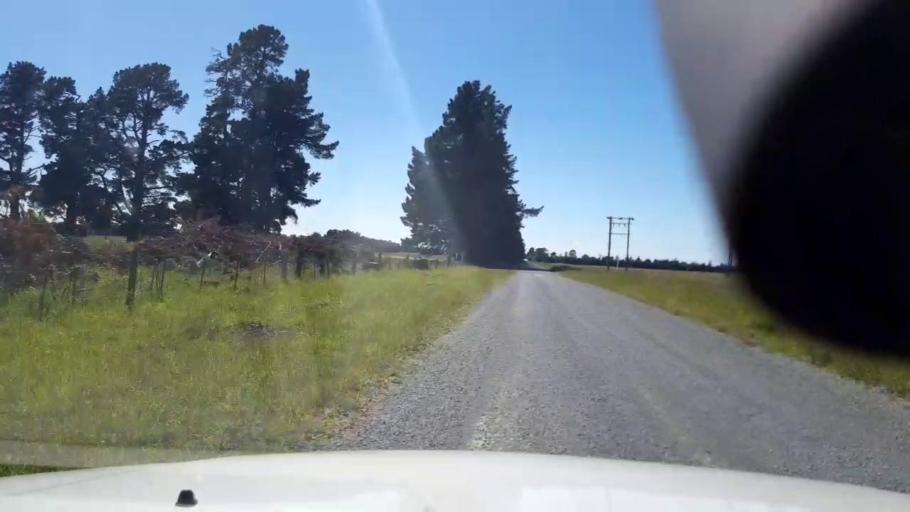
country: NZ
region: Canterbury
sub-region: Timaru District
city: Pleasant Point
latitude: -43.9728
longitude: 171.2497
